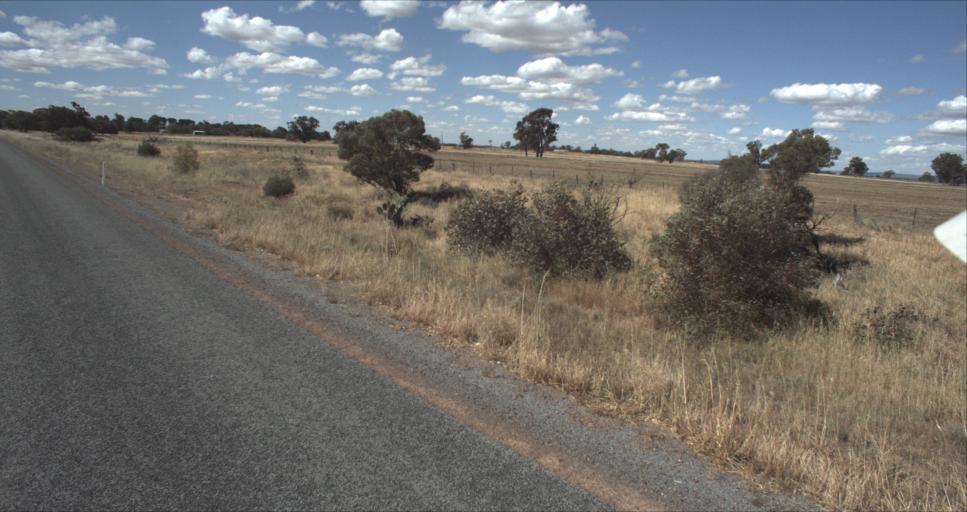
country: AU
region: New South Wales
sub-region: Leeton
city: Leeton
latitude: -34.4912
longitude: 146.2472
